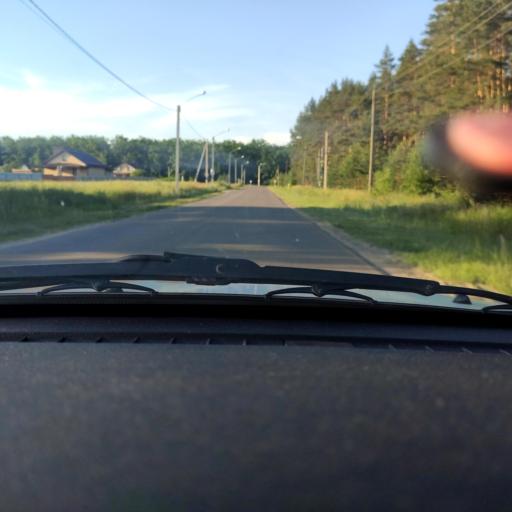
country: RU
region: Voronezj
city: Ramon'
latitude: 51.8937
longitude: 39.2751
